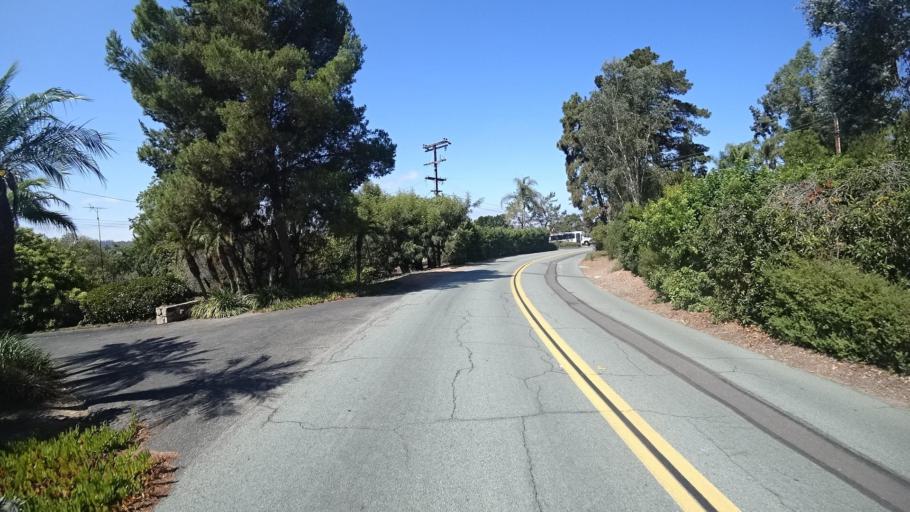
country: US
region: California
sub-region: San Diego County
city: Rancho Santa Fe
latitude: 33.0233
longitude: -117.1960
